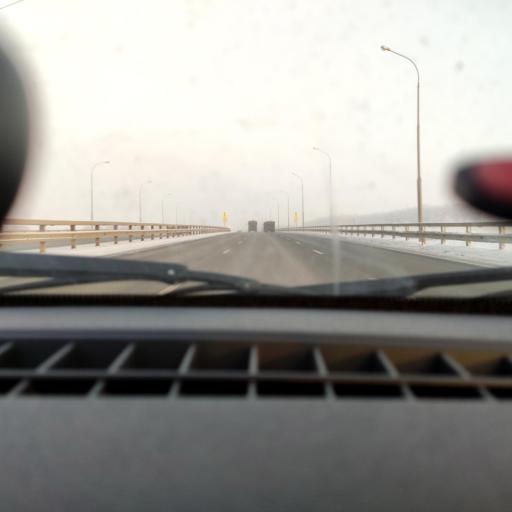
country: RU
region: Bashkortostan
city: Kabakovo
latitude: 54.6521
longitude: 56.1077
